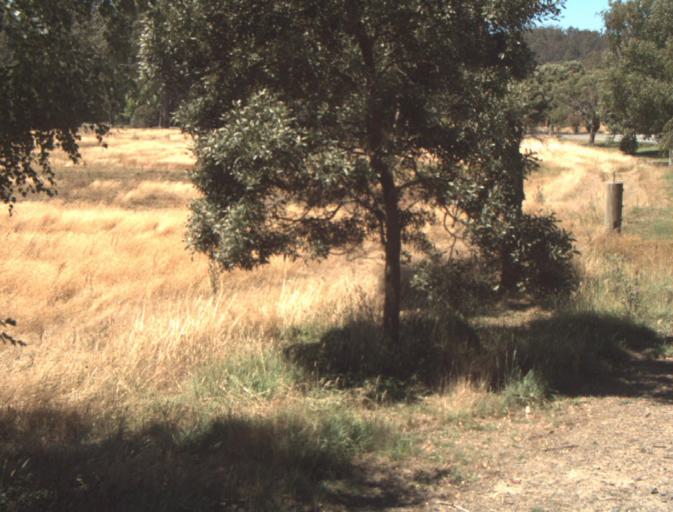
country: AU
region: Tasmania
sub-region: Dorset
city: Scottsdale
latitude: -41.2945
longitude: 147.4042
